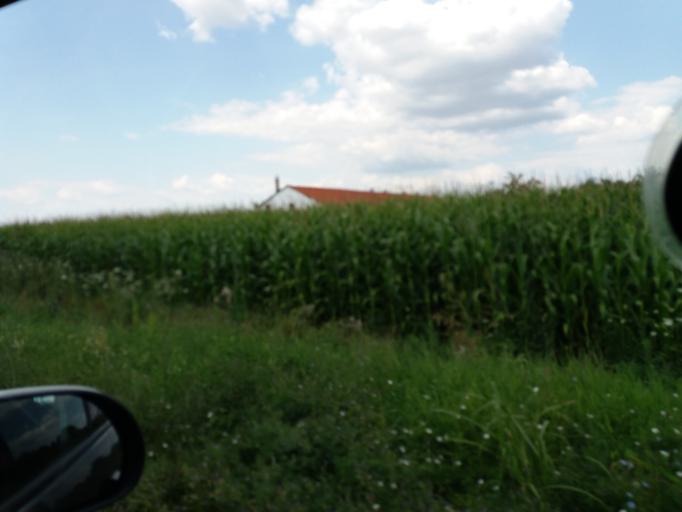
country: RS
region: Autonomna Pokrajina Vojvodina
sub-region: Sremski Okrug
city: Pecinci
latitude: 44.8970
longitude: 19.9661
